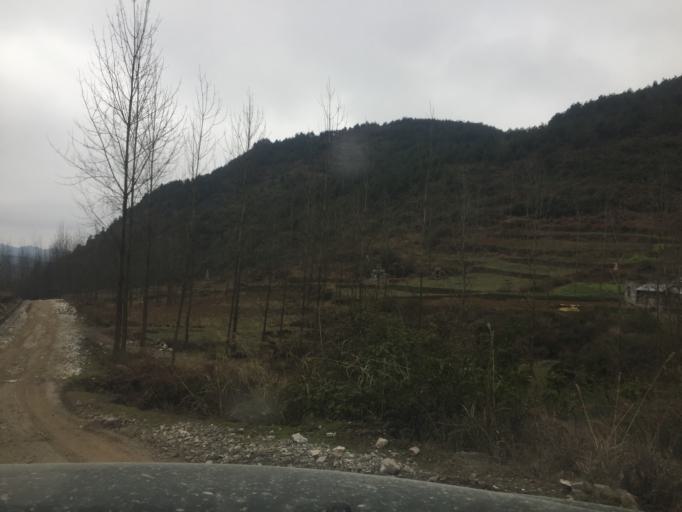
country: CN
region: Guizhou Sheng
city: Jiancha
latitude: 28.1747
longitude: 108.0016
